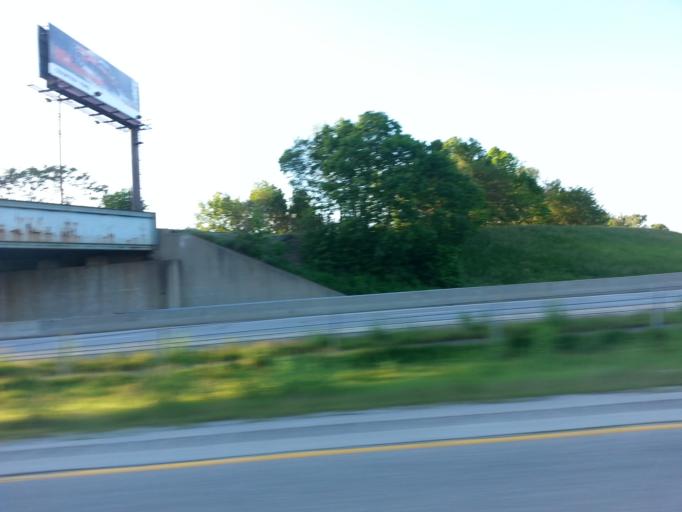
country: US
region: Illinois
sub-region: Vermilion County
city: Tilton
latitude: 40.1048
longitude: -87.6389
